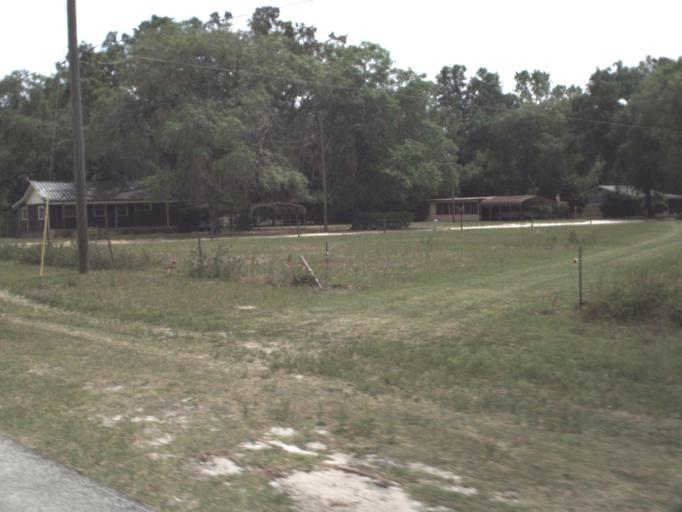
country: US
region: Florida
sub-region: Lake County
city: Mount Dora
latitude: 28.8516
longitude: -81.6262
